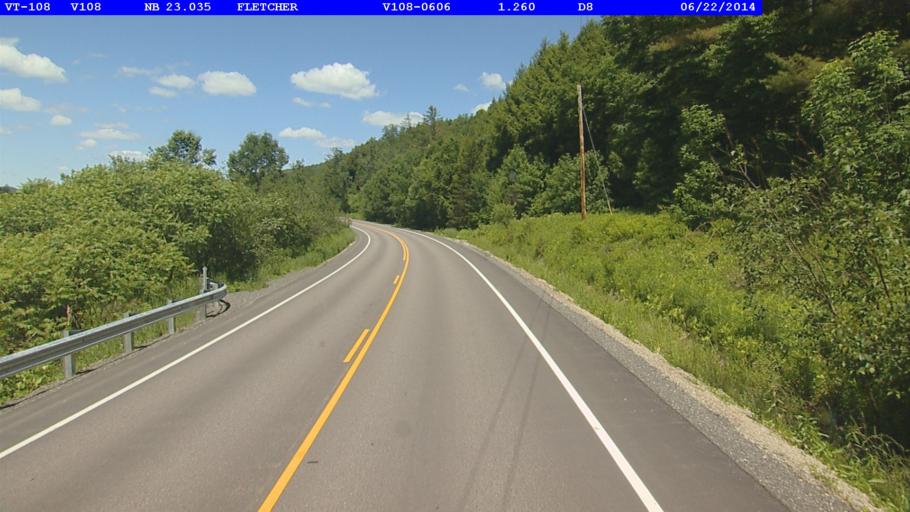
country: US
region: Vermont
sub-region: Lamoille County
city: Johnson
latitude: 44.7186
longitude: -72.8321
